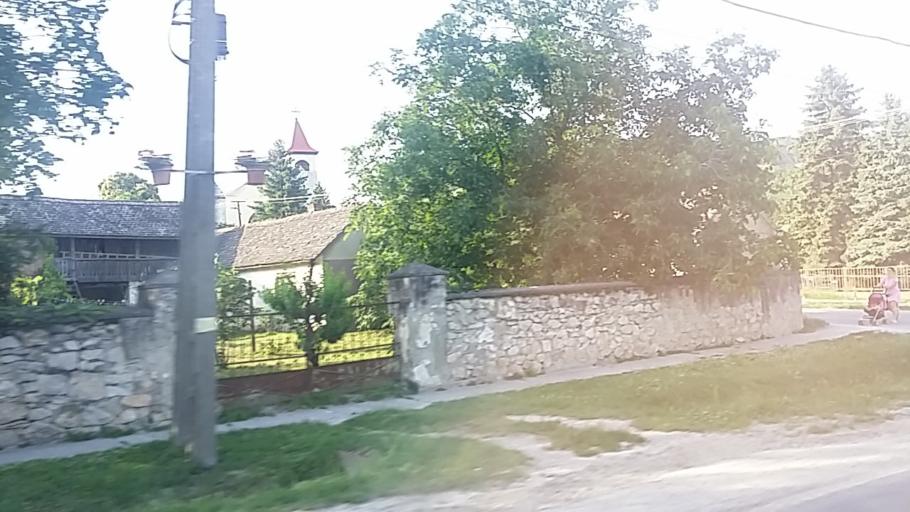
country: HU
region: Baranya
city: Villany
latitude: 45.8480
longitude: 18.3903
